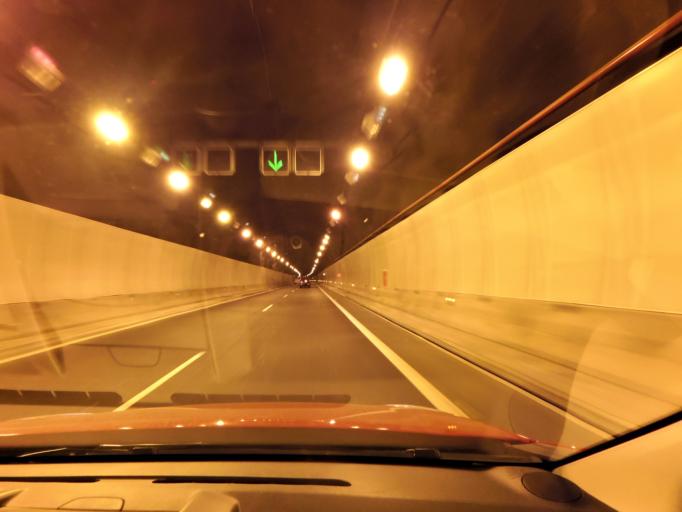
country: ES
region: Canary Islands
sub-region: Provincia de Las Palmas
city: Puerto Rico
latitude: 27.7955
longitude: -15.7003
